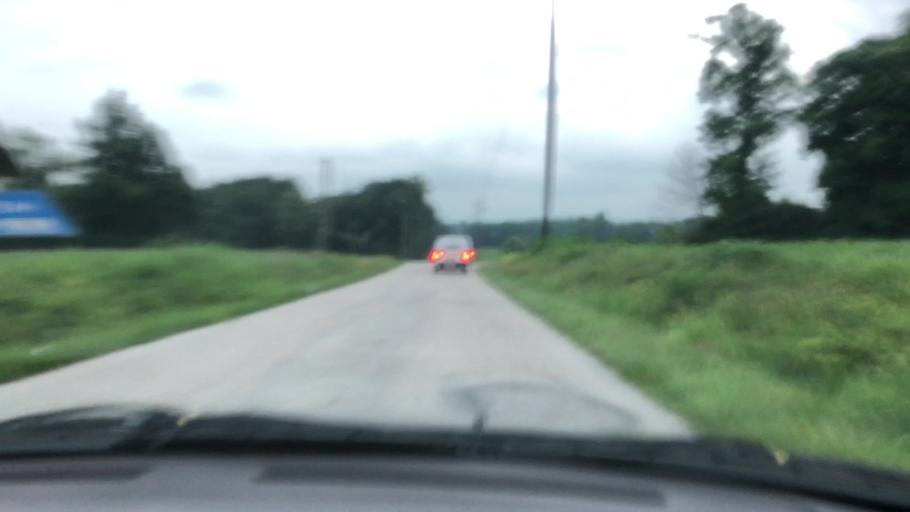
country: US
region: Indiana
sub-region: Greene County
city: Linton
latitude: 38.9837
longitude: -87.2981
